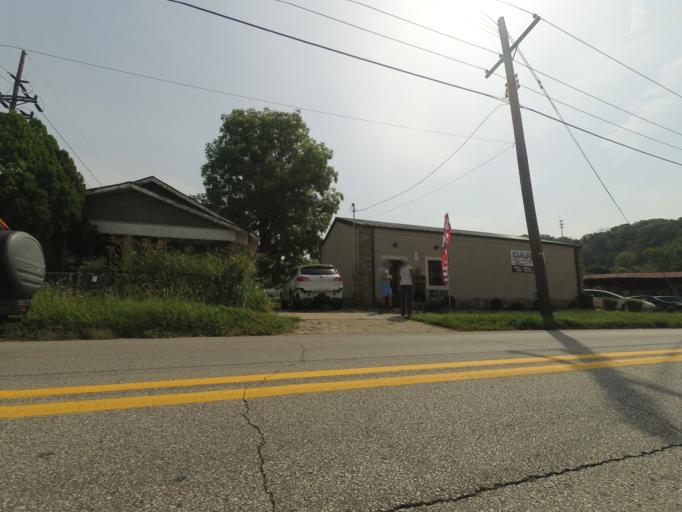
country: US
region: West Virginia
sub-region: Cabell County
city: Huntington
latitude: 38.4066
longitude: -82.4775
